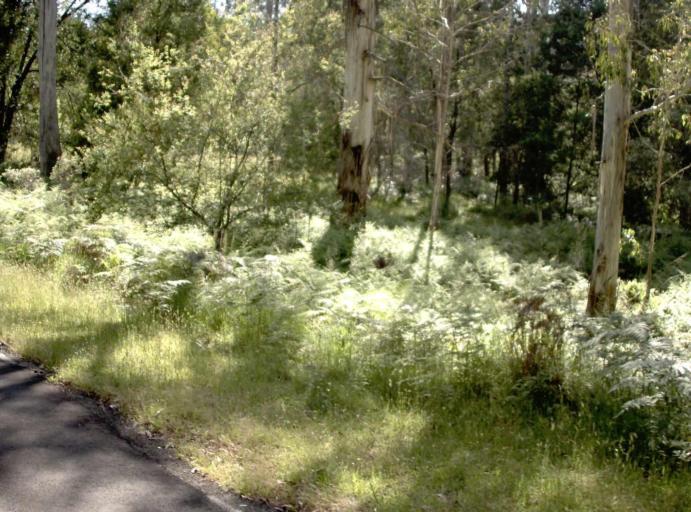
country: AU
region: New South Wales
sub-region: Bombala
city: Bombala
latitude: -37.3699
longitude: 148.6816
